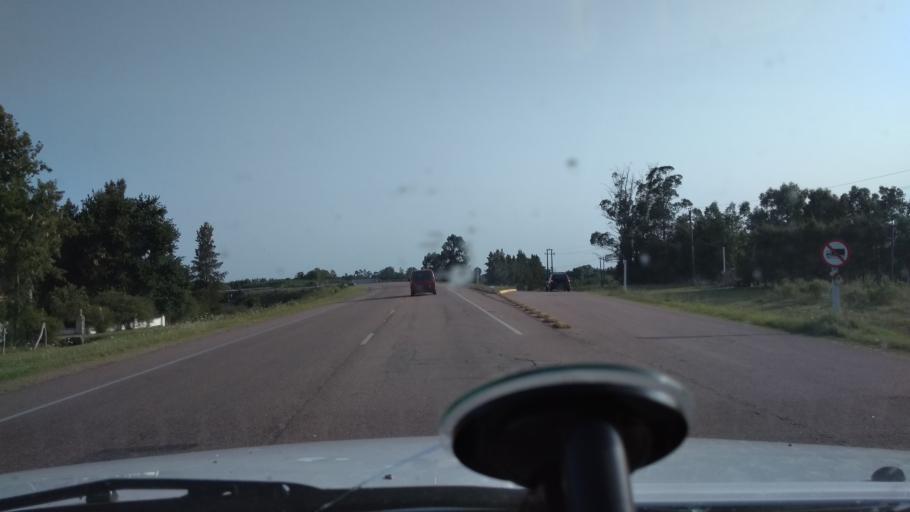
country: UY
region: Canelones
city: Sauce
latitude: -34.6374
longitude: -56.0527
